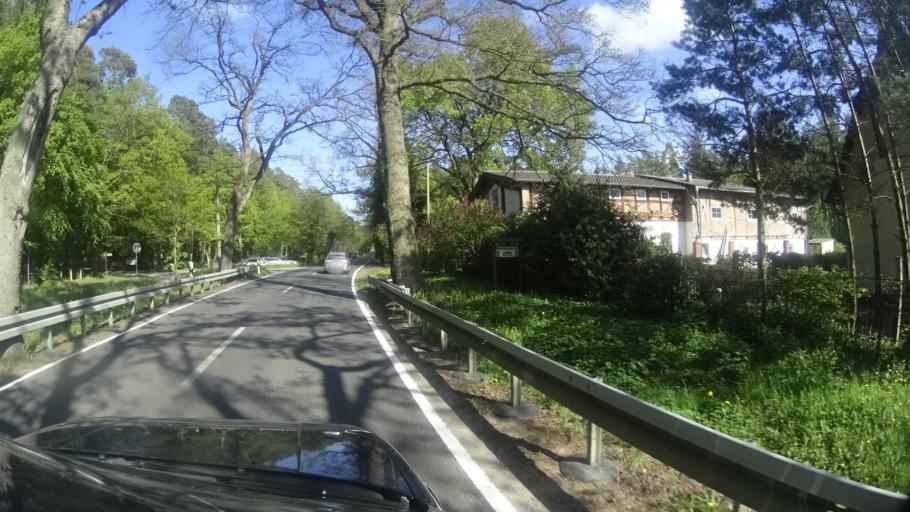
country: DE
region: Mecklenburg-Vorpommern
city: Seeheilbad Graal-Muritz
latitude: 54.2550
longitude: 12.3024
